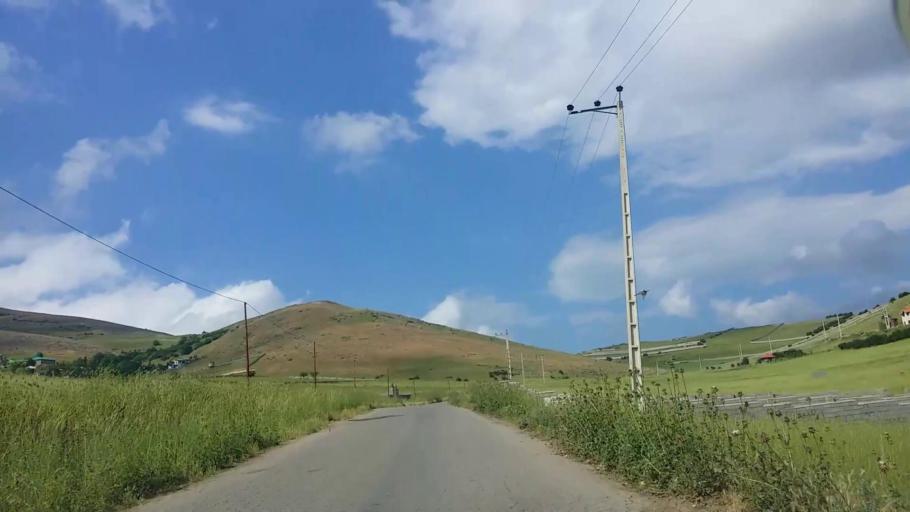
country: IR
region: Mazandaran
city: Chalus
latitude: 36.5231
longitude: 51.2624
